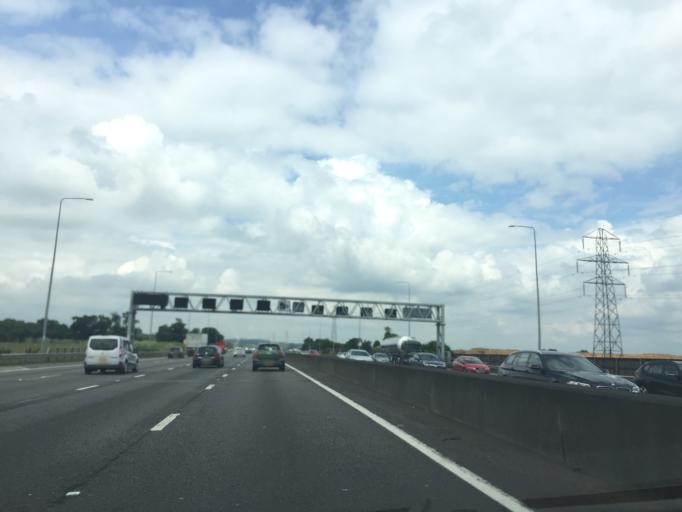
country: GB
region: England
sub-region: Buckinghamshire
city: Gerrards Cross
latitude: 51.5979
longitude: -0.5316
